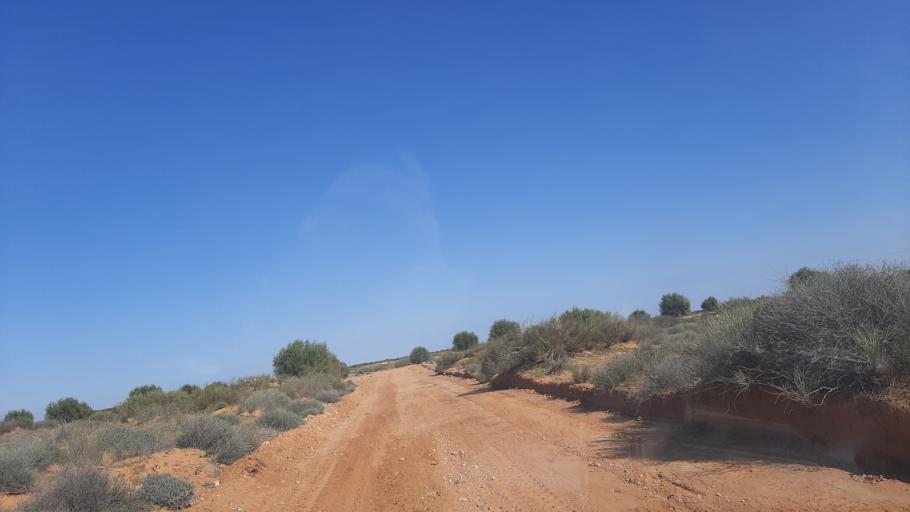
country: TN
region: Madanin
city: Medenine
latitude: 33.2801
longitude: 10.7766
